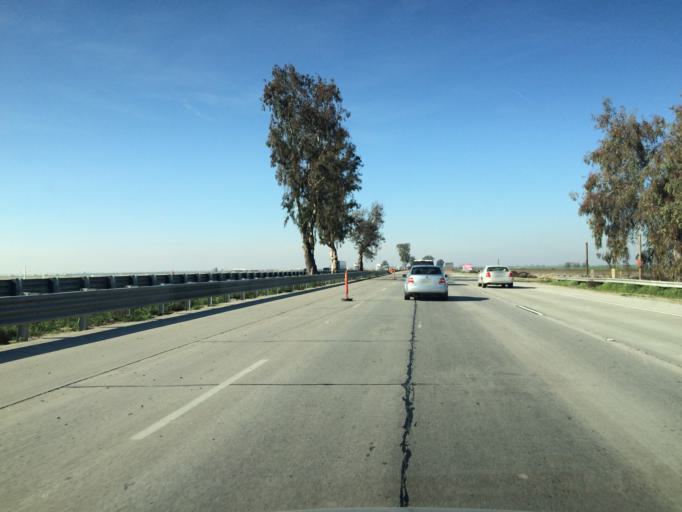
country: US
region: California
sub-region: Tulare County
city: Goshen
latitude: 36.4053
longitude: -119.4569
